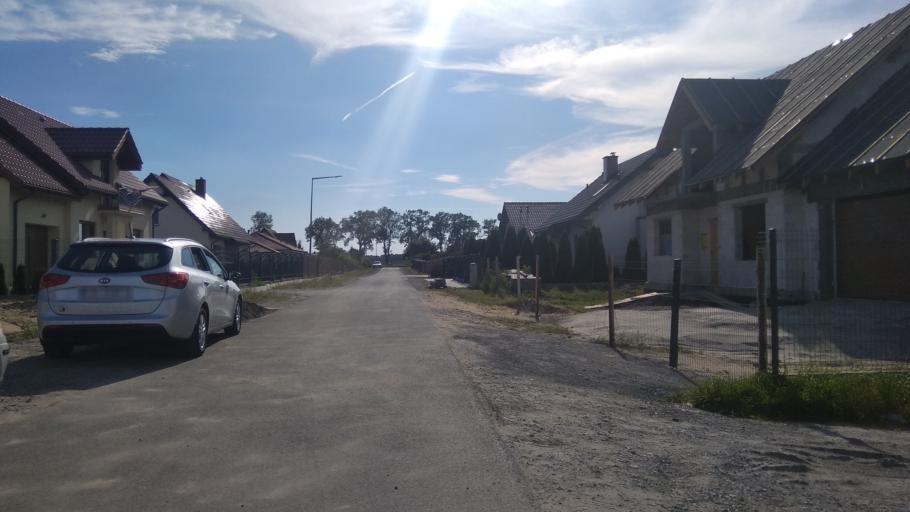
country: PL
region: Kujawsko-Pomorskie
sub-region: Bydgoszcz
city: Fordon
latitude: 53.2153
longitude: 18.1537
